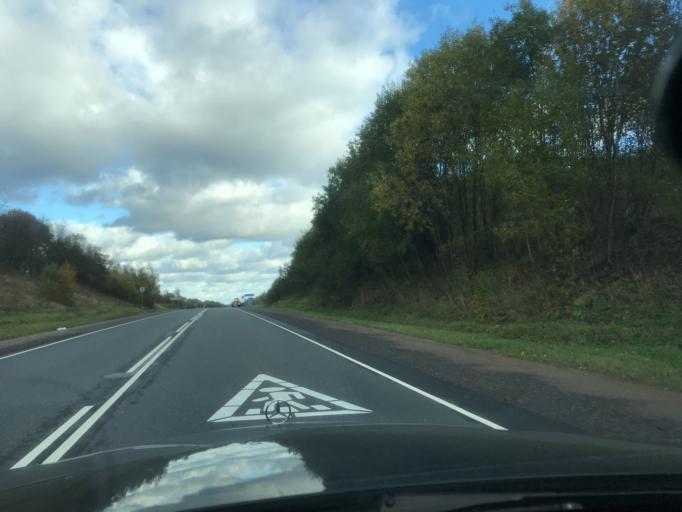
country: RU
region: Pskov
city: Novosokol'niki
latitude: 56.3484
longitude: 29.9039
